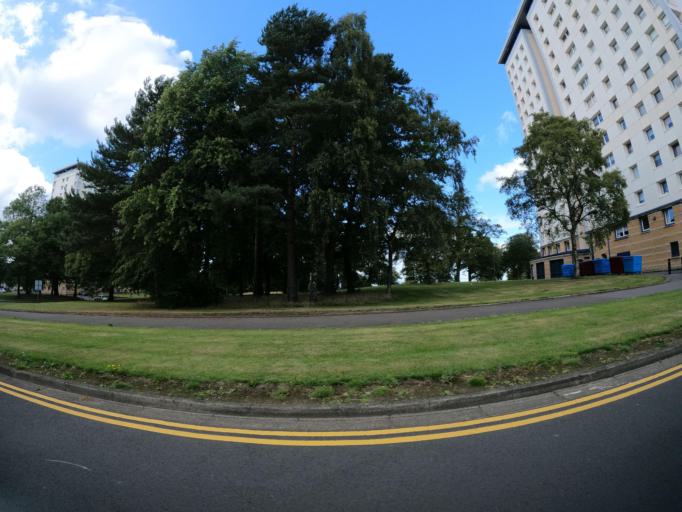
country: GB
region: Scotland
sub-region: Falkirk
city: Falkirk
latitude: 55.9963
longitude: -3.7746
